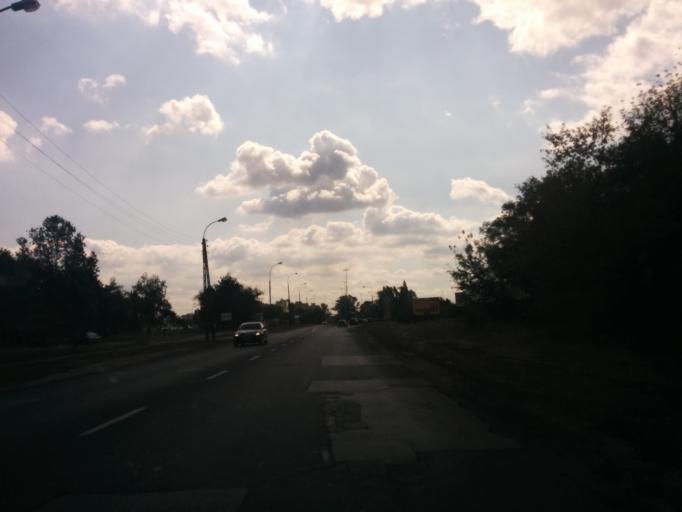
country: PL
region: Masovian Voivodeship
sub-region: Warszawa
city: Targowek
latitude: 52.3009
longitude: 21.0114
